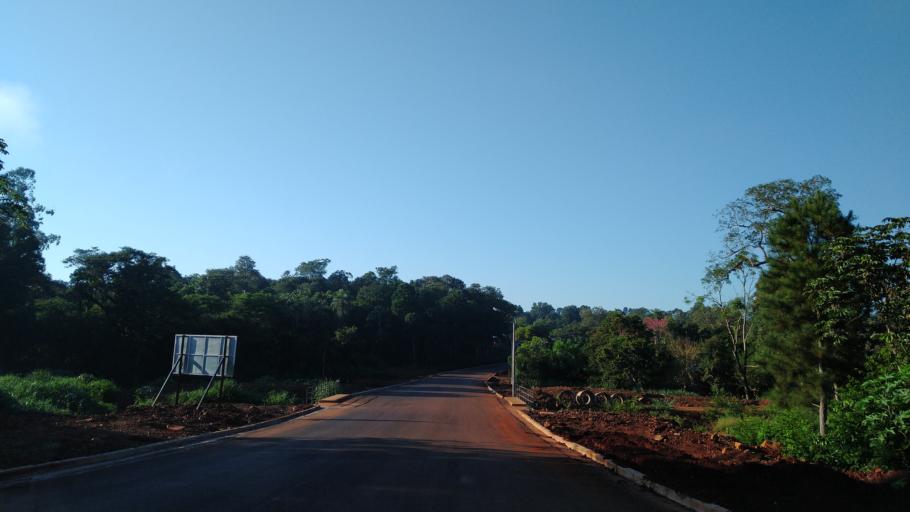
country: AR
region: Misiones
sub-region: Departamento de Montecarlo
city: Montecarlo
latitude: -26.5610
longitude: -54.7697
